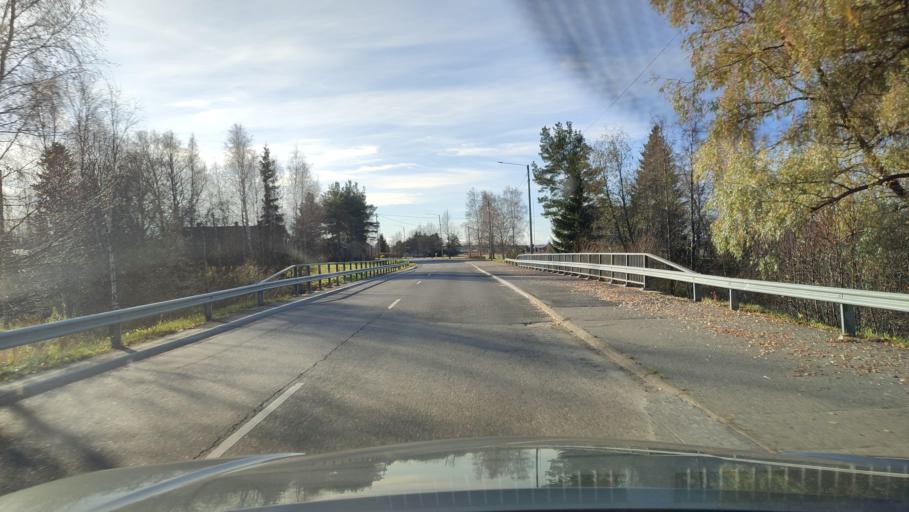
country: FI
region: Southern Ostrobothnia
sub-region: Suupohja
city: Teuva
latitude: 62.4727
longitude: 21.7138
